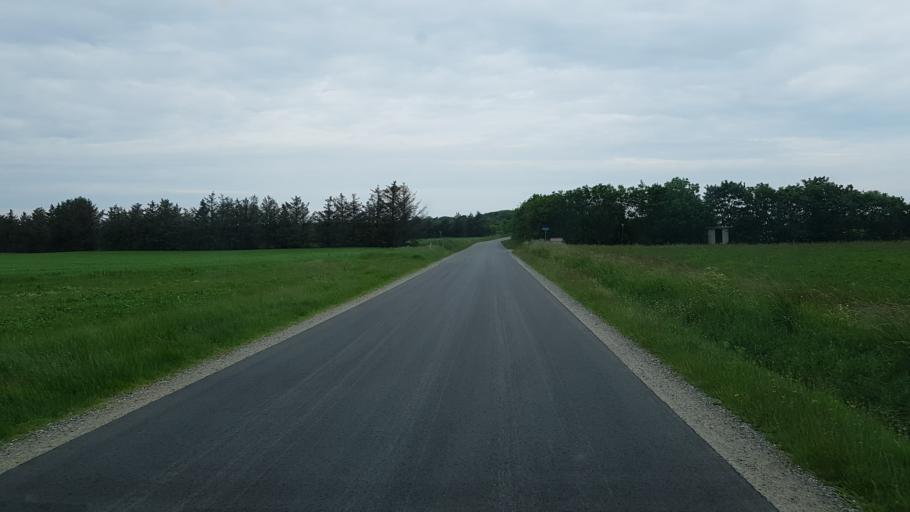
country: DK
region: South Denmark
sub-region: Varde Kommune
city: Oksbol
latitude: 55.7465
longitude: 8.3725
